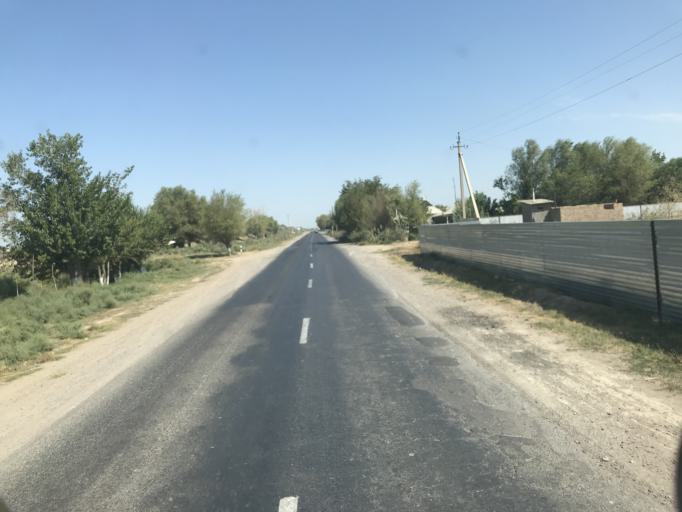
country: KZ
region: Ongtustik Qazaqstan
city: Ilyich
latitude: 40.7660
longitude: 68.5372
